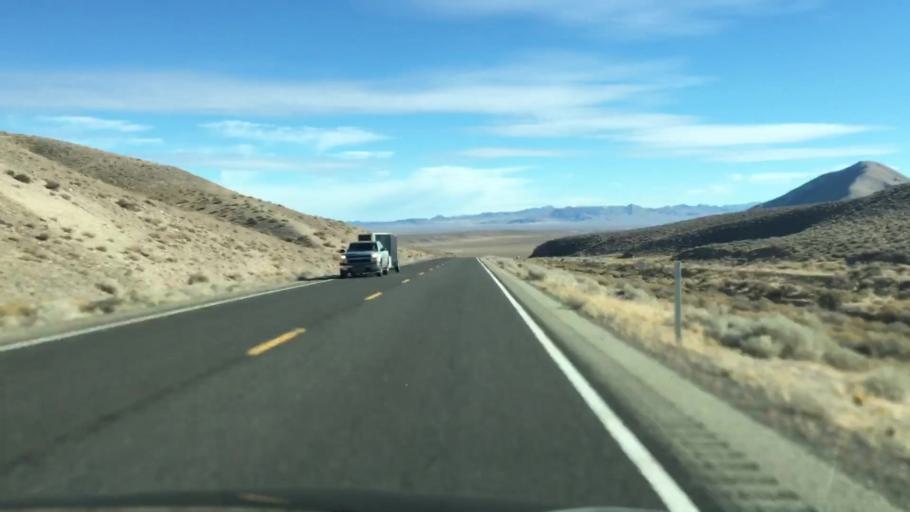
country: US
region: Nevada
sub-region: Lyon County
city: Yerington
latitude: 39.0375
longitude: -118.9317
